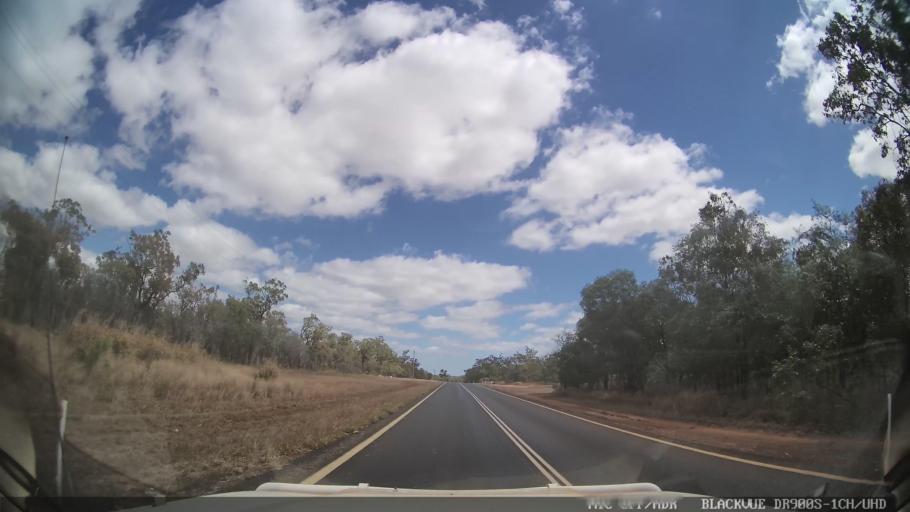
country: AU
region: Queensland
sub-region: Tablelands
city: Ravenshoe
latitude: -17.9101
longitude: 144.8803
